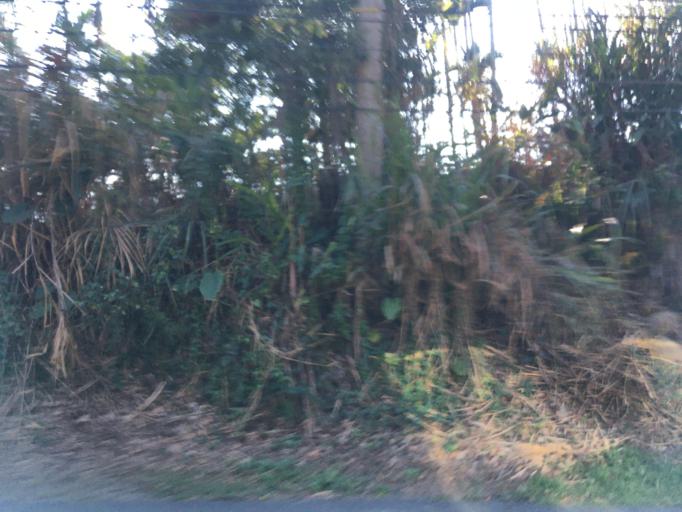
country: TW
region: Taiwan
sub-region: Chiayi
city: Jiayi Shi
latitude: 23.4340
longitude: 120.6325
